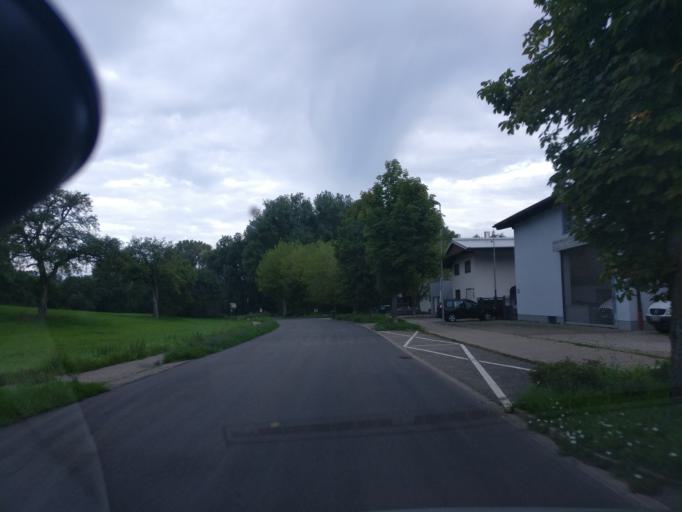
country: DE
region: Baden-Wuerttemberg
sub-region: Karlsruhe Region
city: Joehlingen
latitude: 49.0070
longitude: 8.5598
